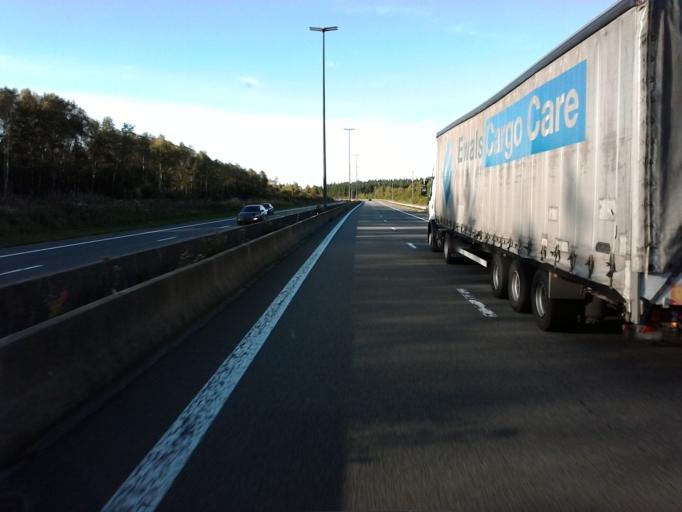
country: BE
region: Wallonia
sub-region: Province de Liege
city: Lierneux
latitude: 50.2232
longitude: 5.7715
